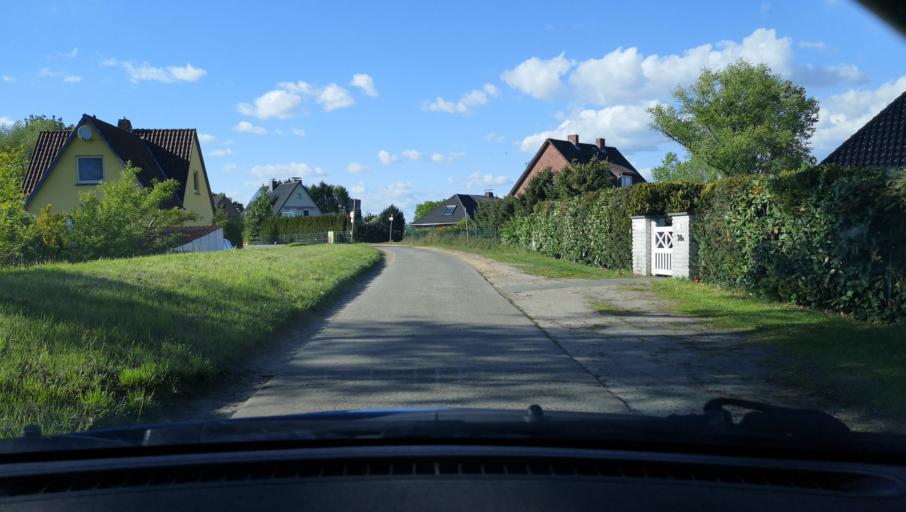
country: DE
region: Lower Saxony
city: Stelle
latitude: 53.3809
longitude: 10.1237
